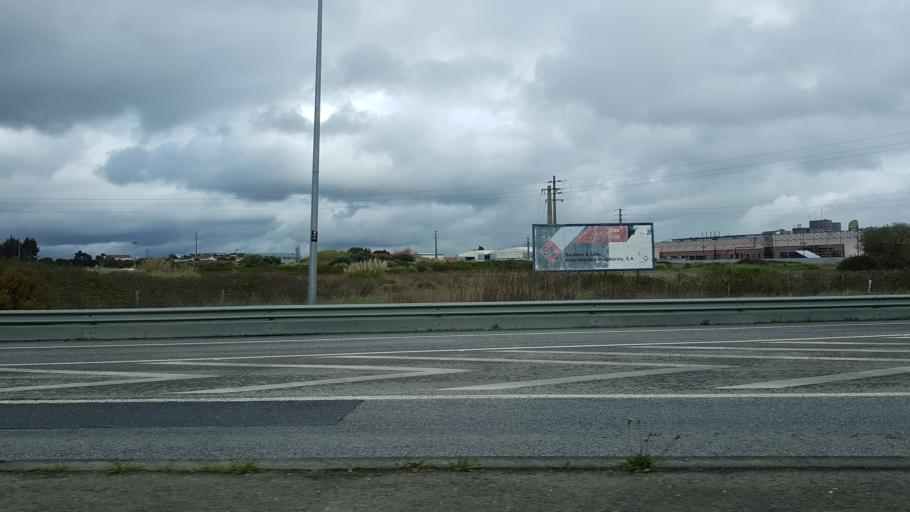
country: PT
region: Lisbon
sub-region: Alenquer
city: Carregado
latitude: 39.0352
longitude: -8.9821
